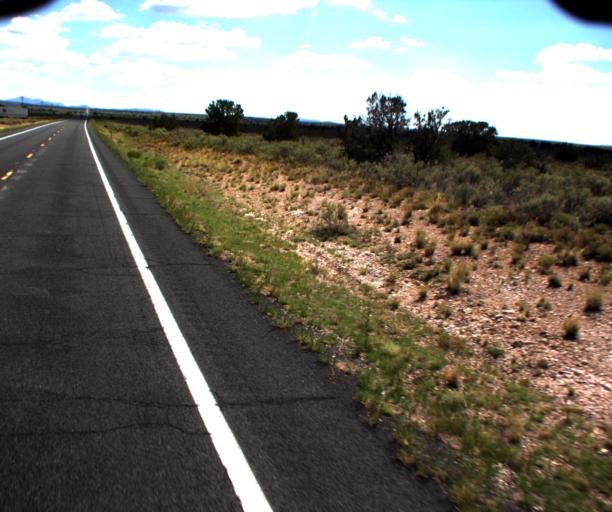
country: US
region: Arizona
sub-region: Coconino County
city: Williams
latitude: 35.6014
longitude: -112.1470
